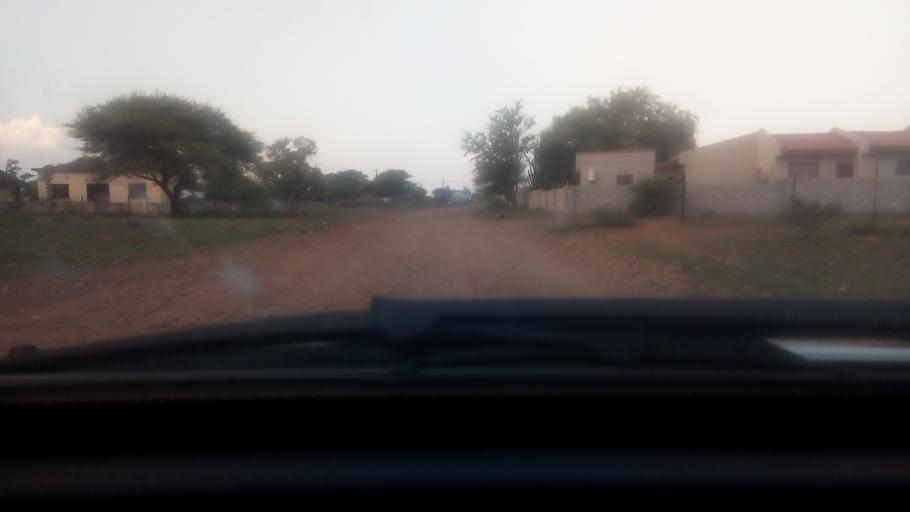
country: BW
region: Kgatleng
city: Bokaa
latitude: -24.4278
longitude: 26.0152
